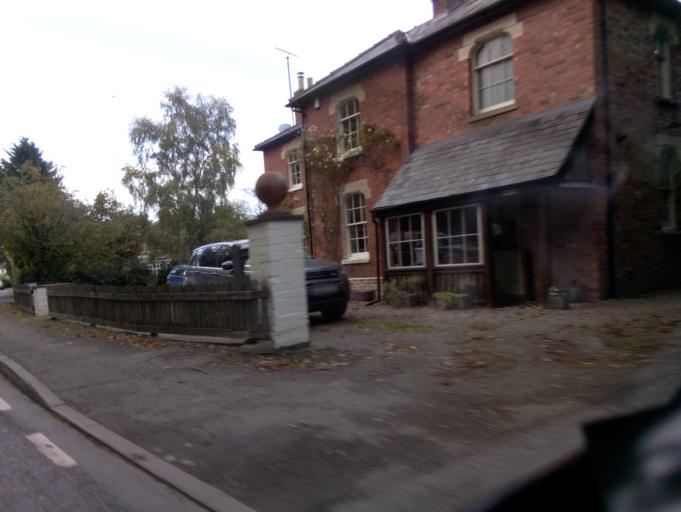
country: GB
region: England
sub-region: Herefordshire
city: Ocle Pychard
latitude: 52.0649
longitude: -2.5555
